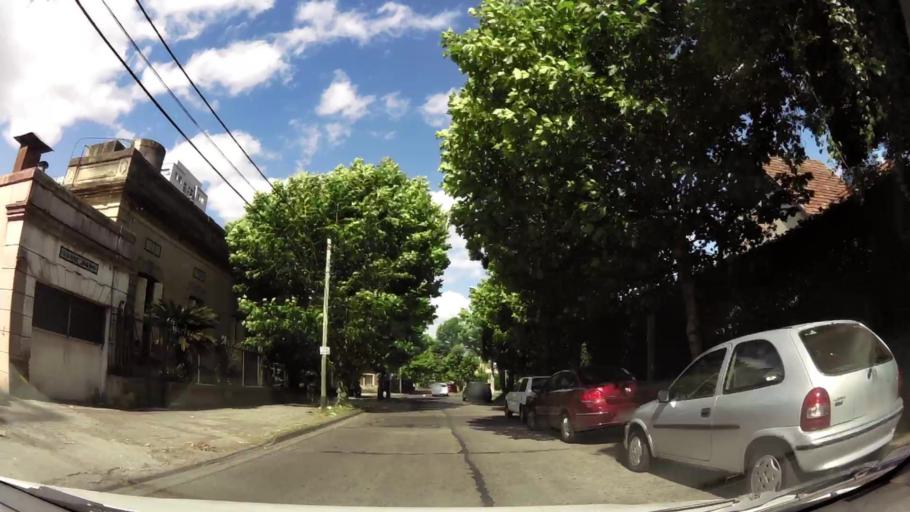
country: AR
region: Buenos Aires
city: San Justo
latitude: -34.6410
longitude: -58.5575
